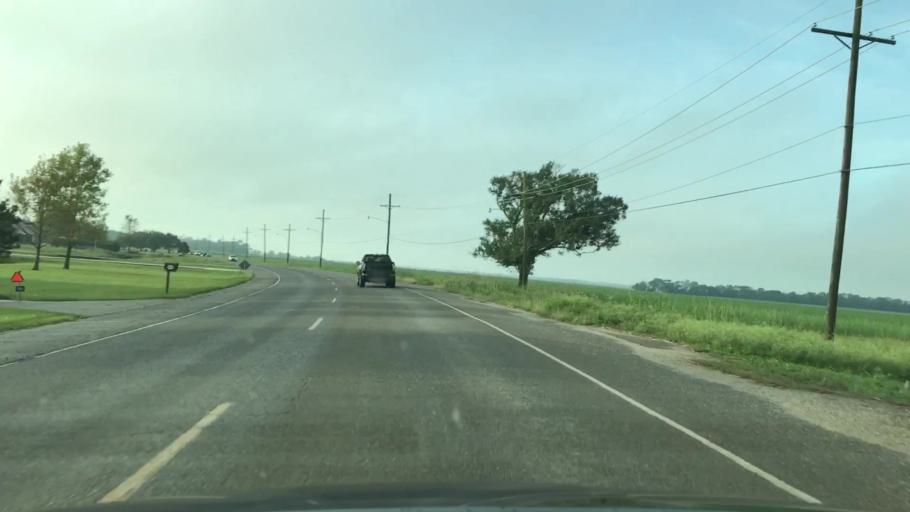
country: US
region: Louisiana
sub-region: Terrebonne Parish
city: Gray
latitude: 29.6630
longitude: -90.8202
